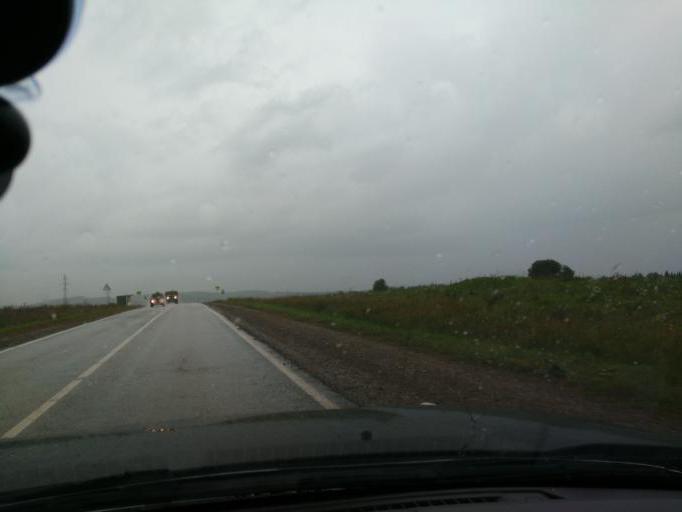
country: RU
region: Perm
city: Barda
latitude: 57.0943
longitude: 55.5342
